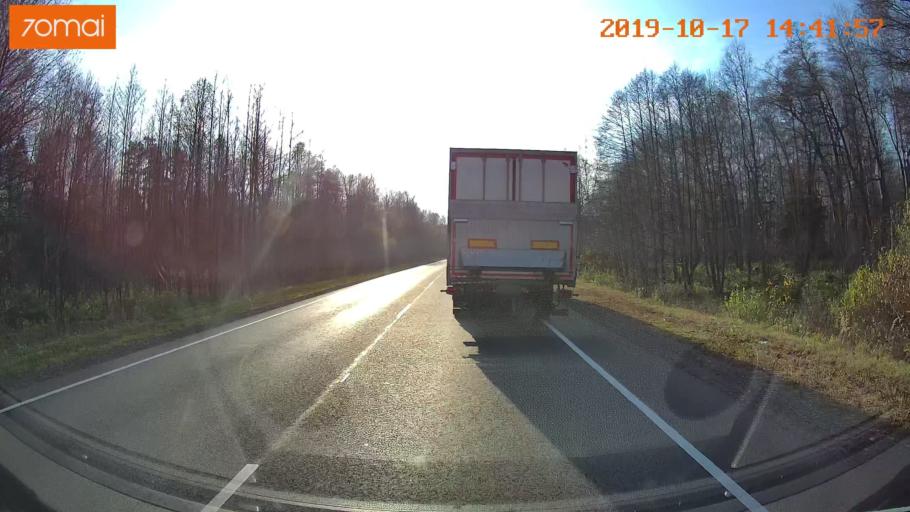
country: RU
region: Rjazan
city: Solotcha
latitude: 54.8414
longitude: 39.9331
